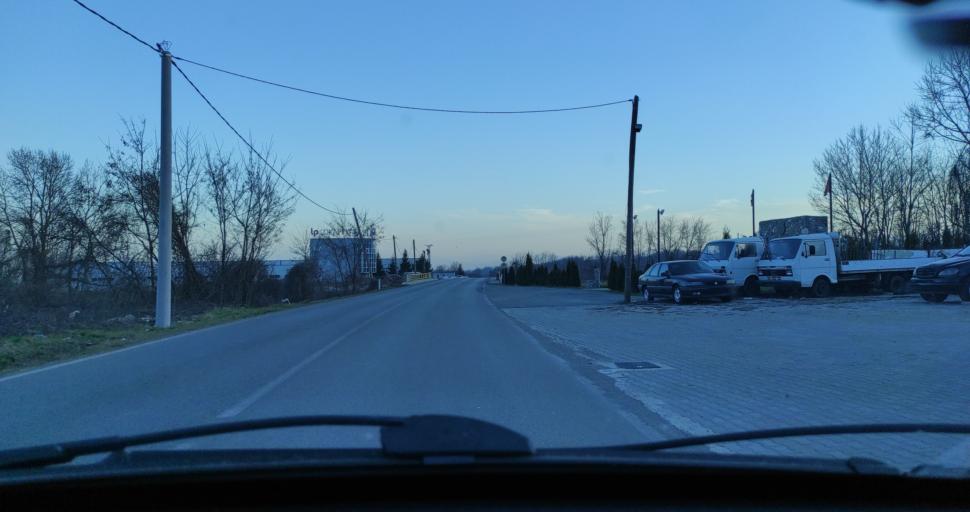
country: XK
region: Gjakova
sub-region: Komuna e Decanit
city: Dranoc
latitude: 42.5190
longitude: 20.3056
